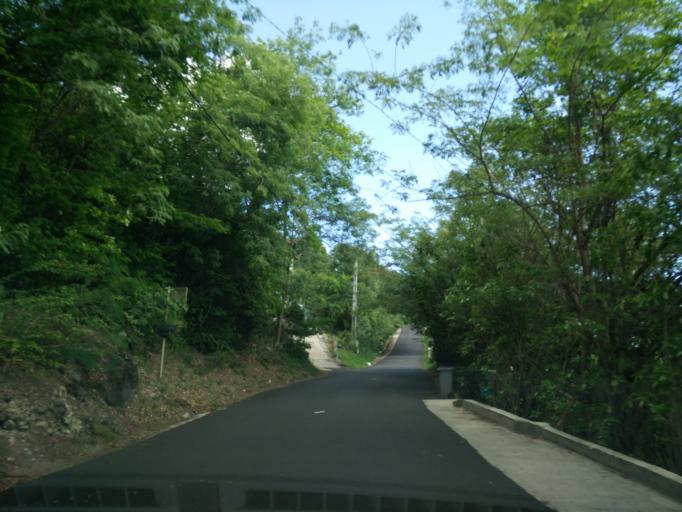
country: MQ
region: Martinique
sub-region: Martinique
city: Les Trois-Ilets
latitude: 14.4864
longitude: -61.0791
